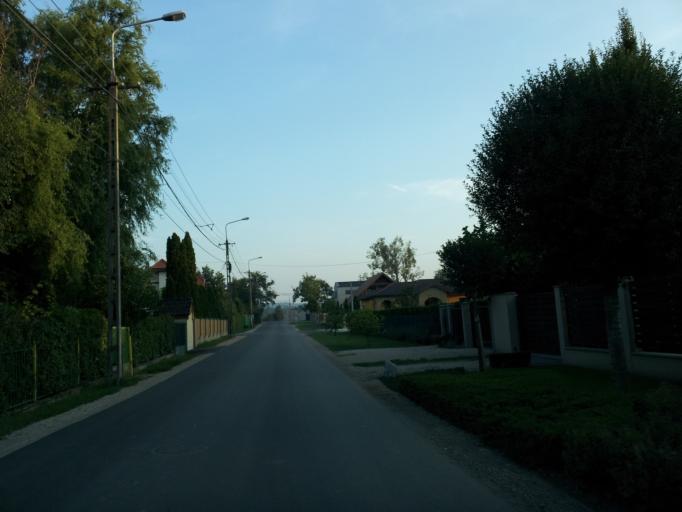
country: HU
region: Somogy
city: Zamardi
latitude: 46.8818
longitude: 17.9223
